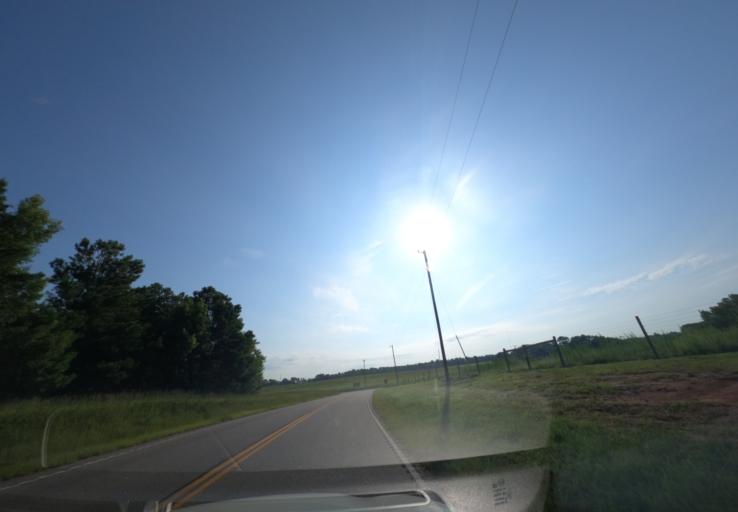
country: US
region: South Carolina
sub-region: Edgefield County
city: Murphys Estates
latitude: 33.6131
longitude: -81.9662
